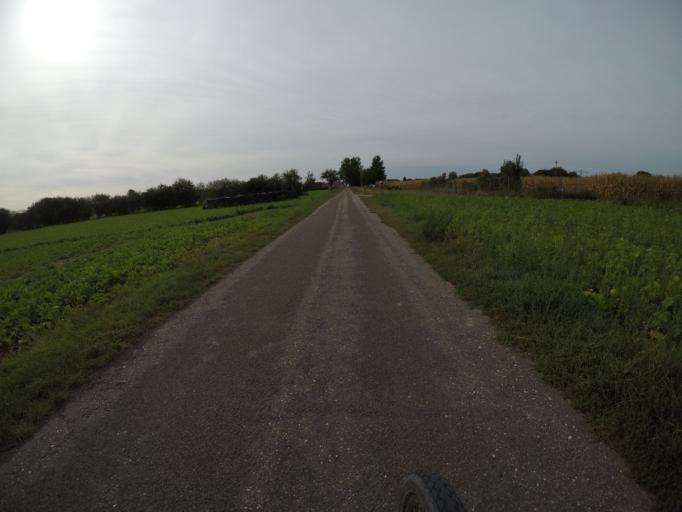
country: DE
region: Baden-Wuerttemberg
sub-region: Karlsruhe Region
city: Kronau
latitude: 49.2298
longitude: 8.6300
